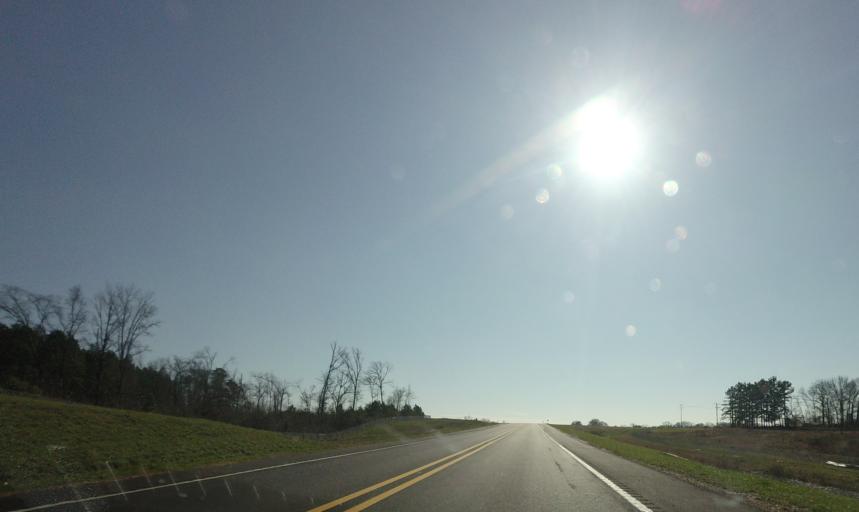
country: US
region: Mississippi
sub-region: Marshall County
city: Byhalia
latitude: 34.8987
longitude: -89.6896
